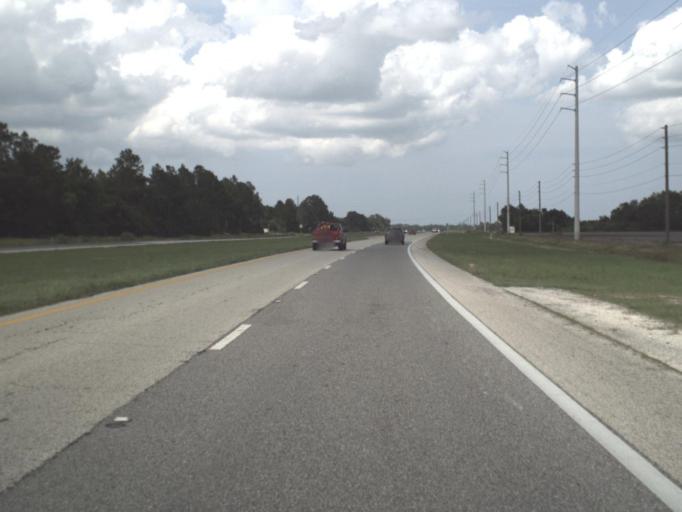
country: US
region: Florida
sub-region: Putnam County
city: East Palatka
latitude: 29.6923
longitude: -81.5653
